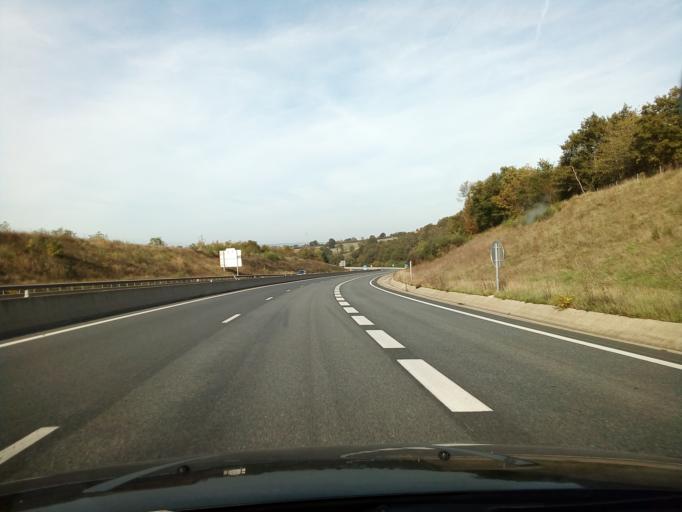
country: FR
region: Auvergne
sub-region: Departement de l'Allier
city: Desertines
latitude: 46.3722
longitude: 2.6299
